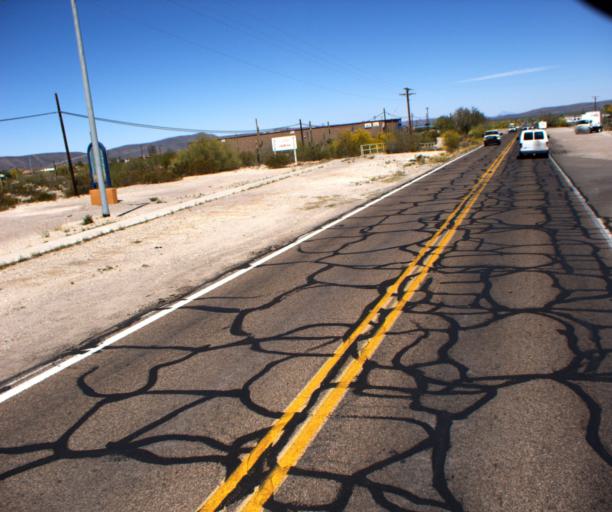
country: US
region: Arizona
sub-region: Pima County
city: Ajo
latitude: 32.3904
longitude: -112.8722
